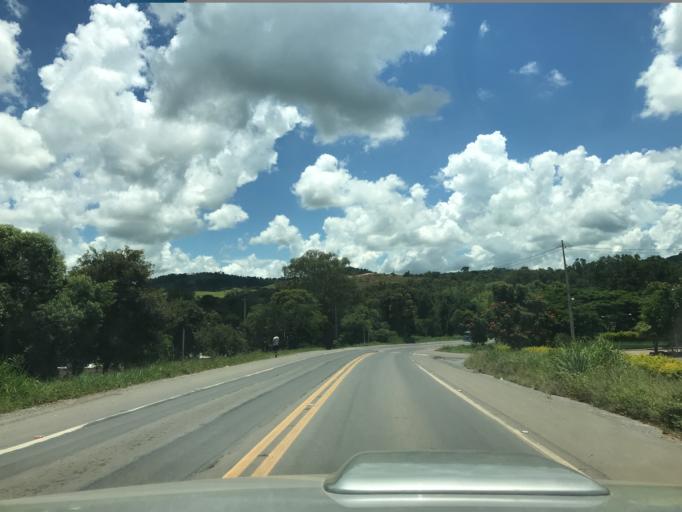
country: BR
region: Minas Gerais
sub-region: Perdoes
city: Perdoes
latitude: -21.0979
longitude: -45.1002
